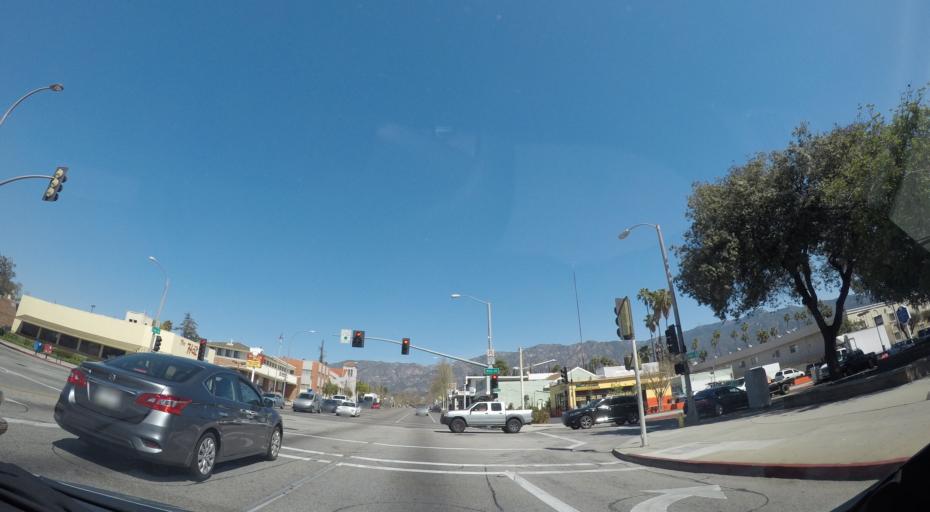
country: US
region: California
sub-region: Los Angeles County
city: Pasadena
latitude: 34.1541
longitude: -118.1324
